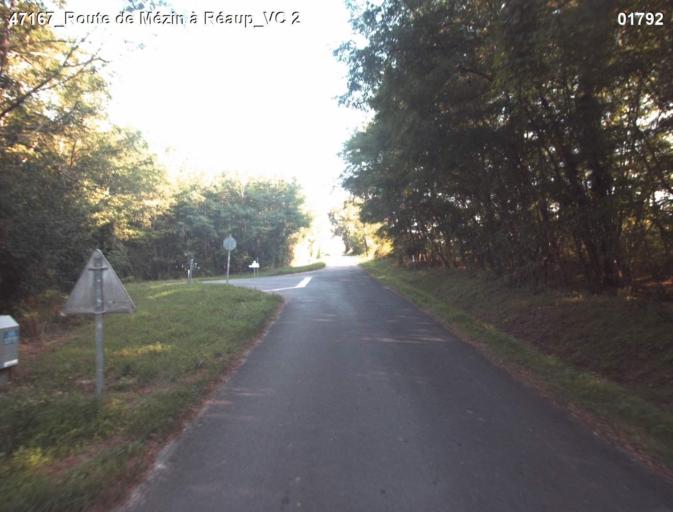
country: FR
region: Aquitaine
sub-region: Departement du Lot-et-Garonne
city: Mezin
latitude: 44.0730
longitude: 0.2535
